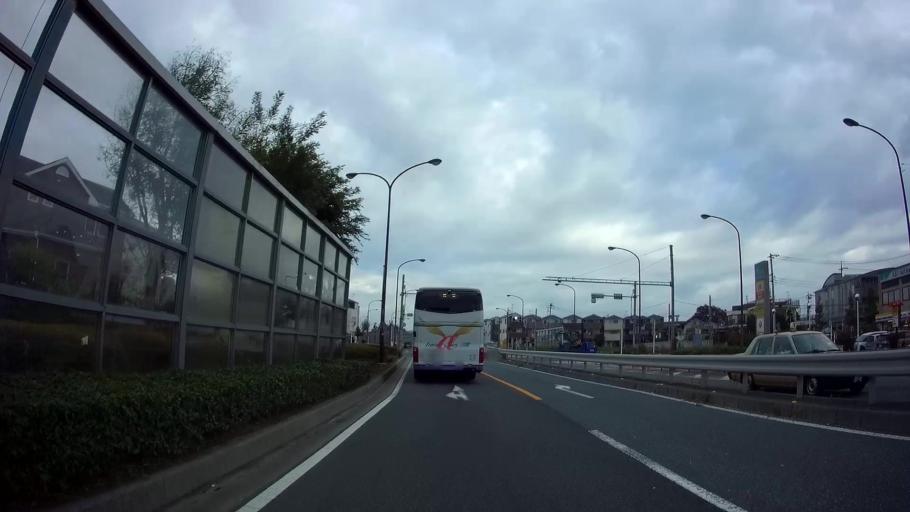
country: JP
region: Saitama
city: Wako
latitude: 35.7798
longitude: 139.6501
